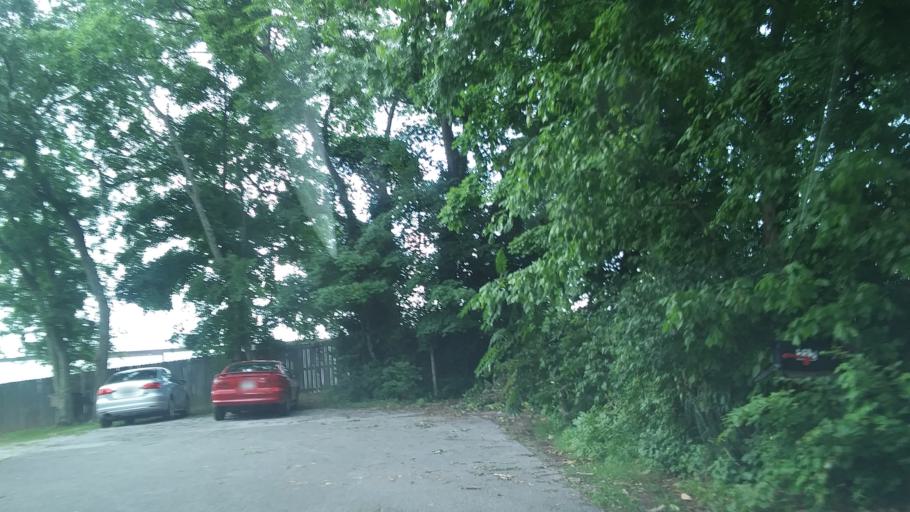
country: US
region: Tennessee
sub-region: Davidson County
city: Oak Hill
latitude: 36.0744
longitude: -86.6970
